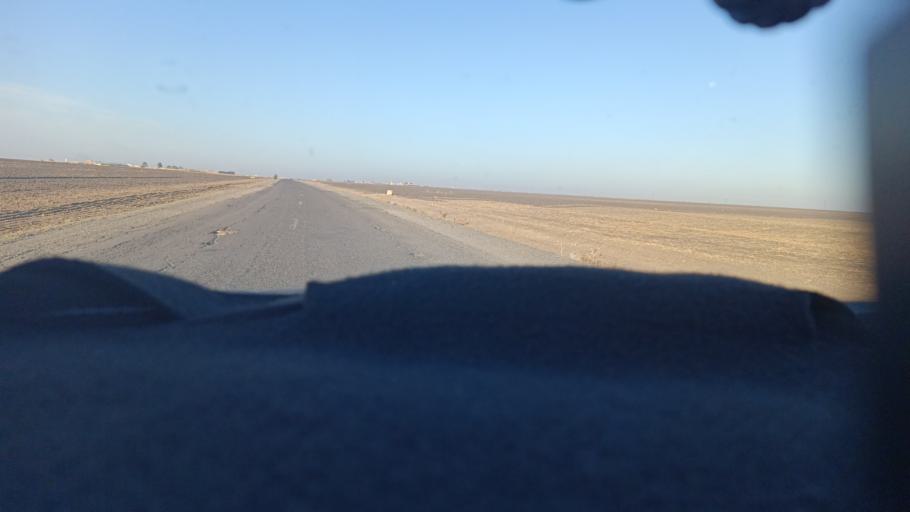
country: MA
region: Doukkala-Abda
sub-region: Safi
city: Youssoufia
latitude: 32.3672
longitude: -8.7446
